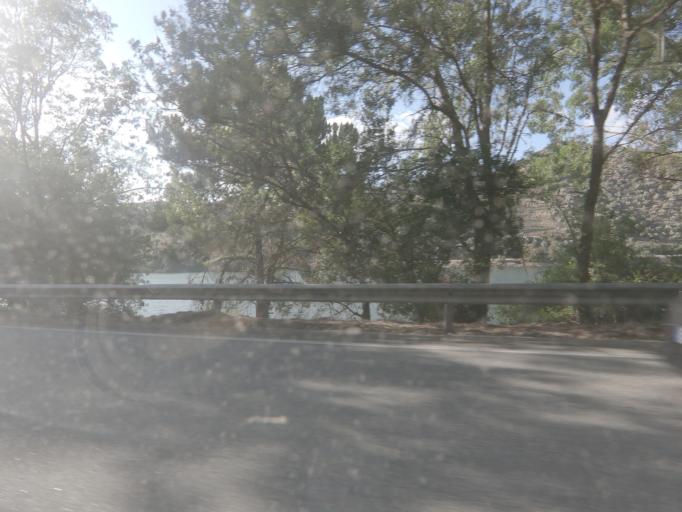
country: PT
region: Vila Real
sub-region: Sabrosa
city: Vilela
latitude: 41.1572
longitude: -7.6306
